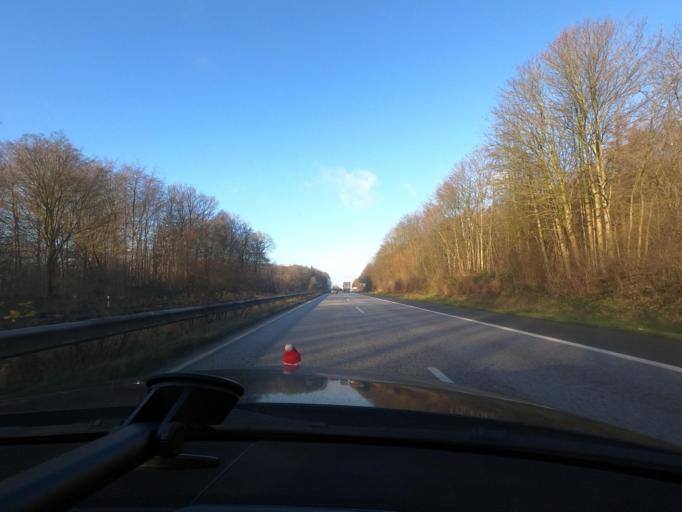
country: DE
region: Schleswig-Holstein
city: Schuby
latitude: 54.5109
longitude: 9.4988
